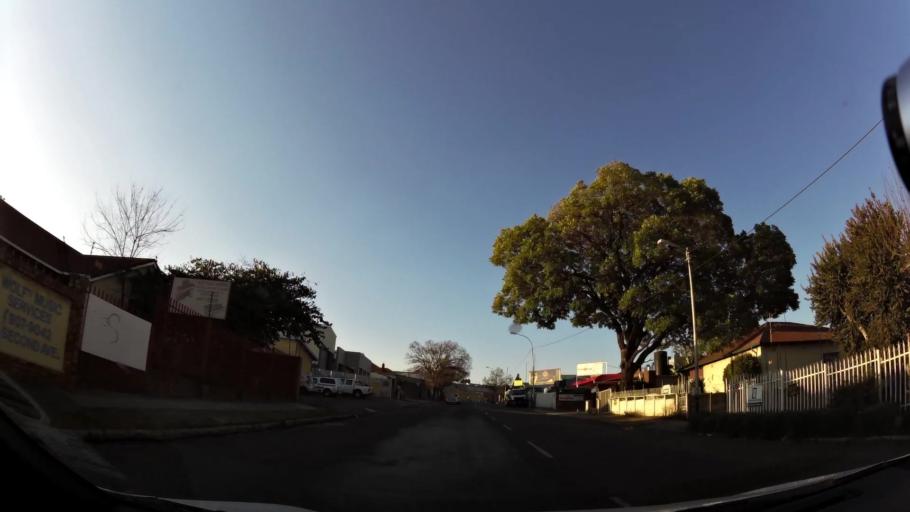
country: ZA
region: Gauteng
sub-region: Ekurhuleni Metropolitan Municipality
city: Germiston
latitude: -26.2538
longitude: 28.1317
